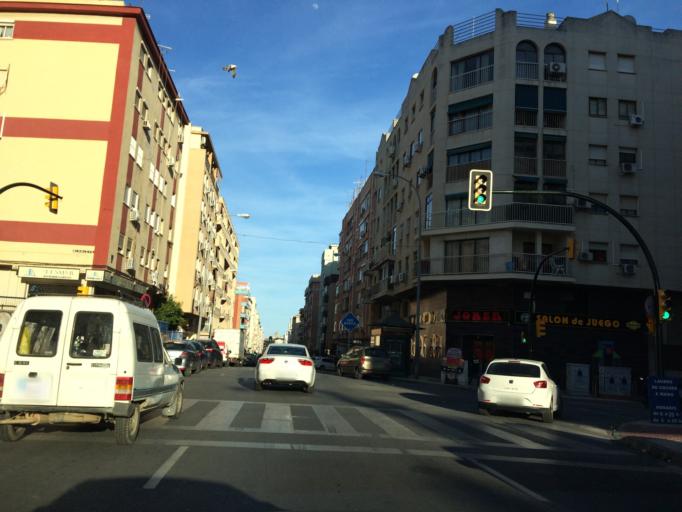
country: ES
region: Andalusia
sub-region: Provincia de Malaga
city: Malaga
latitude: 36.7284
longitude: -4.4444
